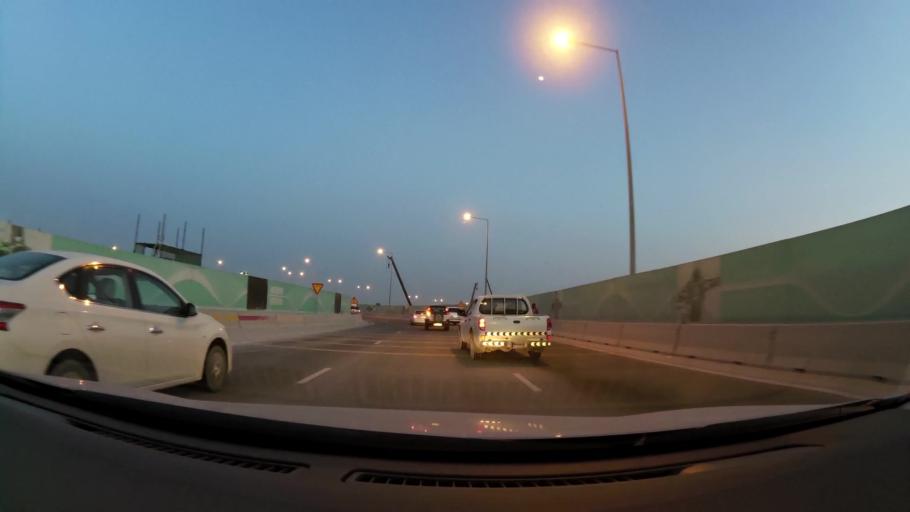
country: QA
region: Baladiyat ar Rayyan
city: Ar Rayyan
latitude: 25.3188
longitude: 51.4480
